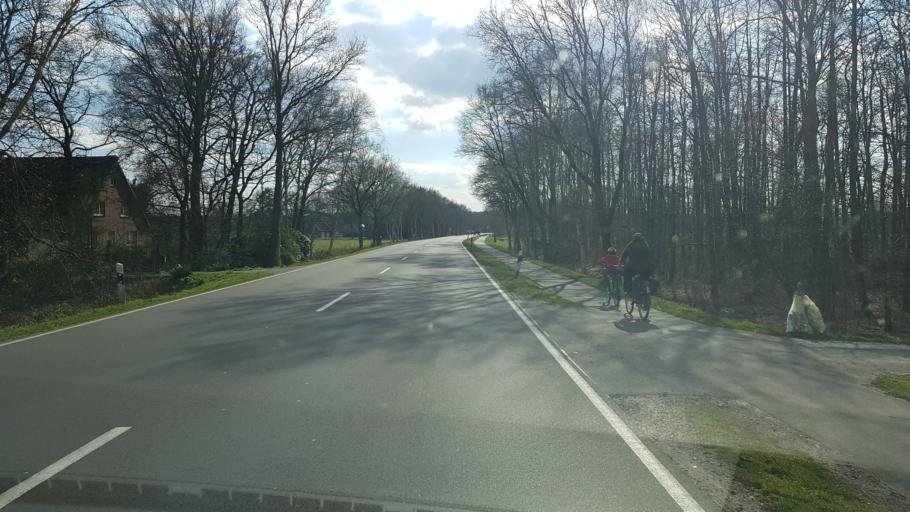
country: DE
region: Lower Saxony
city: Rastede
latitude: 53.2394
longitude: 8.2845
